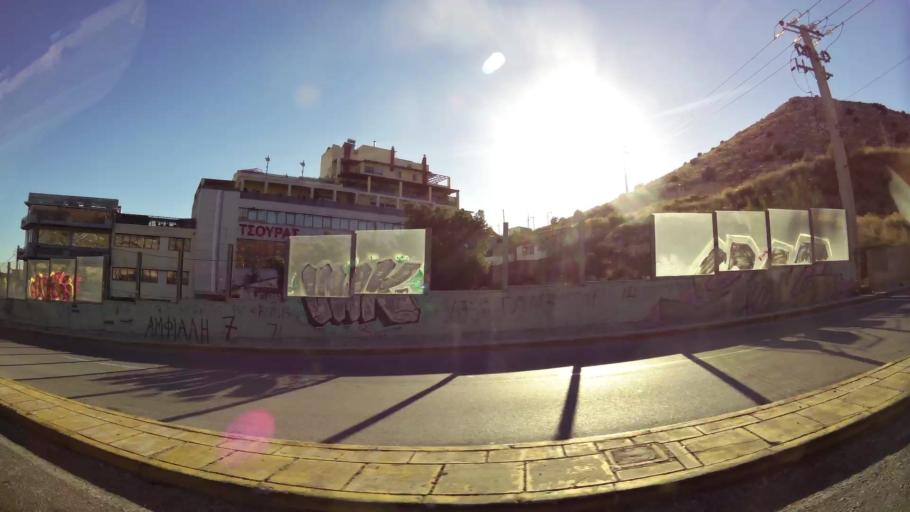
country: GR
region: Attica
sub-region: Nomos Piraios
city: Keratsini
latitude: 37.9671
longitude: 23.6068
